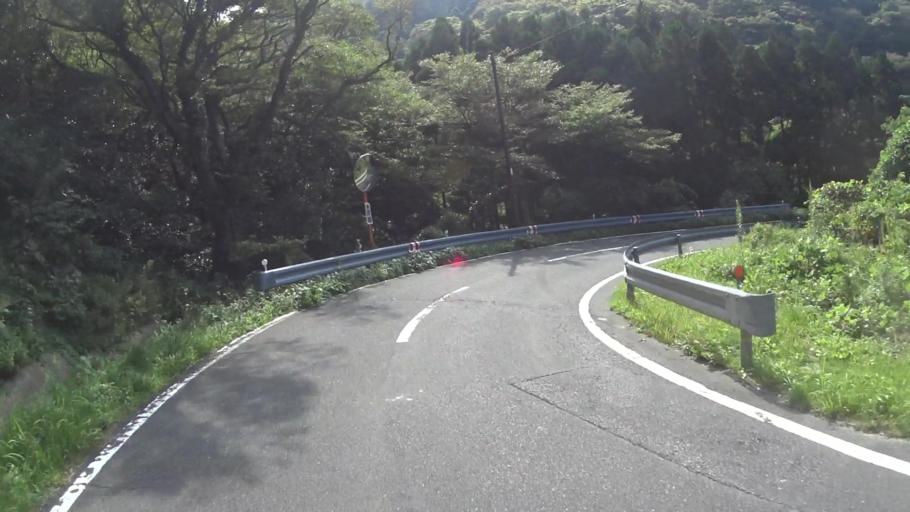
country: JP
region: Kyoto
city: Miyazu
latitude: 35.7679
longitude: 135.2264
